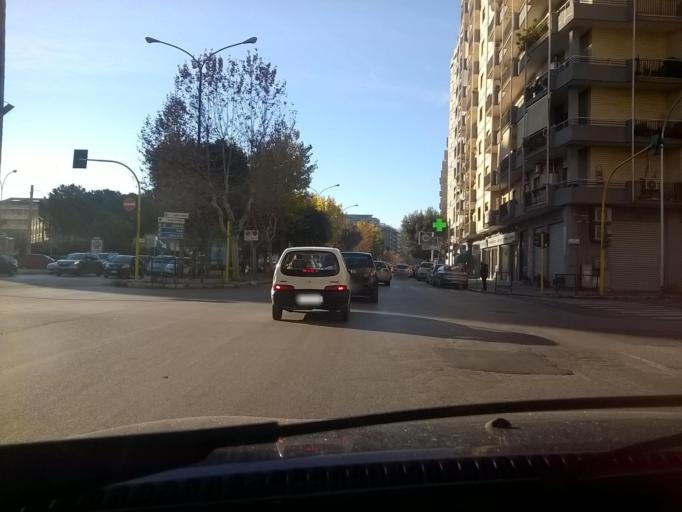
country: IT
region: Apulia
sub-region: Provincia di Taranto
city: Taranto
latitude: 40.4623
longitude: 17.2689
